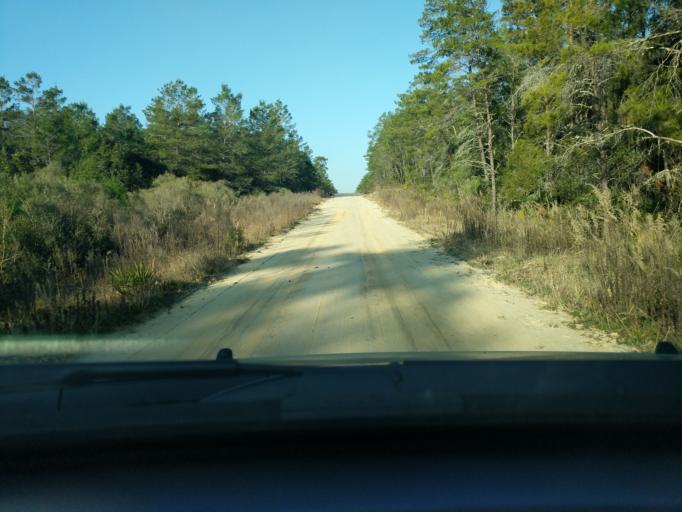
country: US
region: Florida
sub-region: Lake County
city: Astor
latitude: 29.2260
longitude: -81.7605
